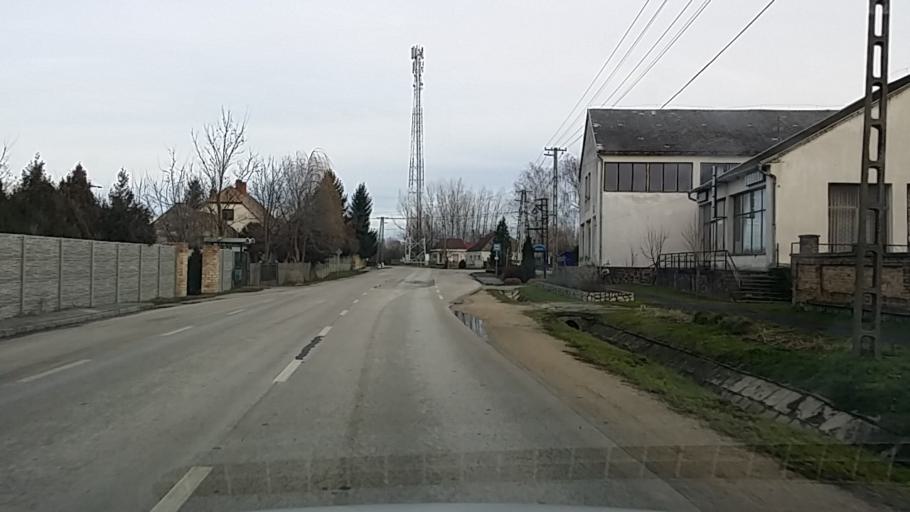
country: HU
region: Gyor-Moson-Sopron
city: Bakonyszentlaszlo
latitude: 47.3861
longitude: 17.7003
